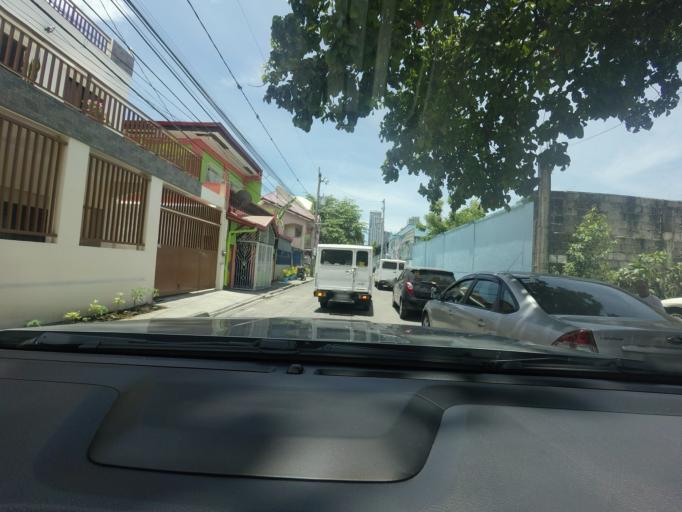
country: PH
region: Metro Manila
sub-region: Marikina
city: Calumpang
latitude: 14.6139
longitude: 121.0859
